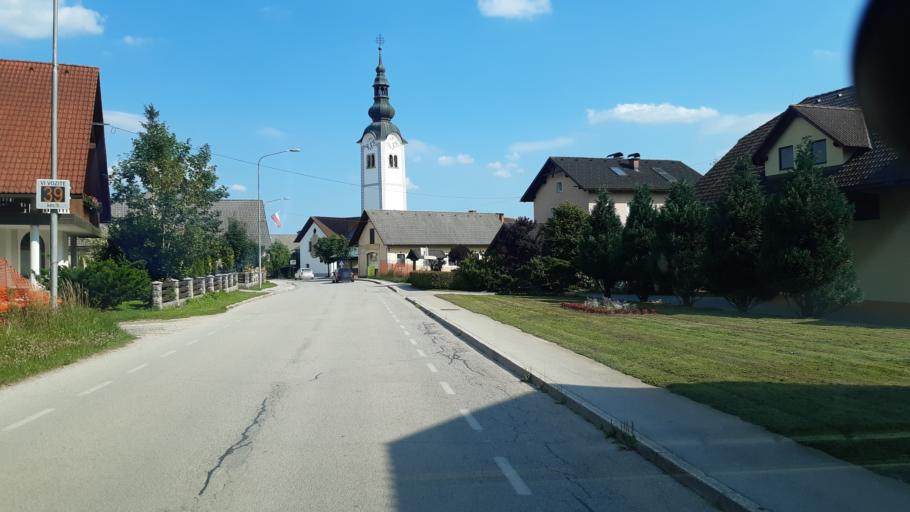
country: SI
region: Sencur
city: Hrastje
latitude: 46.2189
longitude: 14.3847
